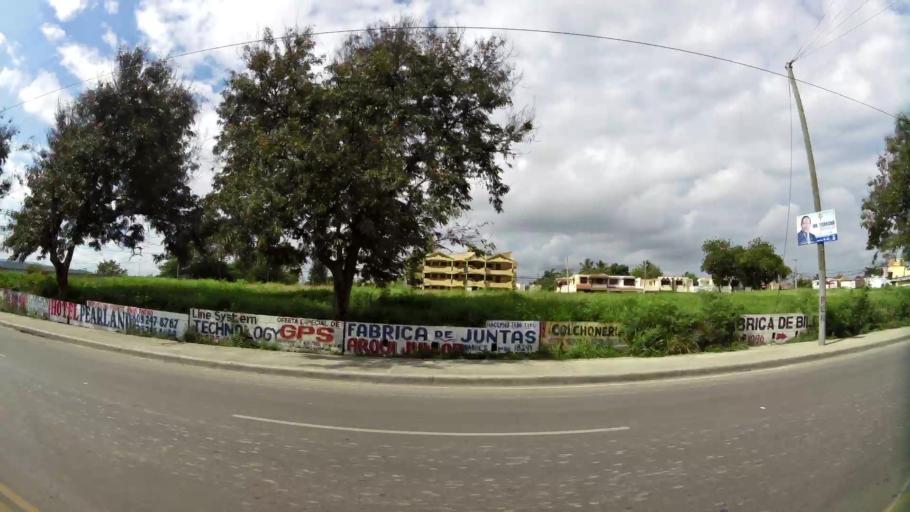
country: DO
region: Santiago
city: Santiago de los Caballeros
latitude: 19.4757
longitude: -70.7229
